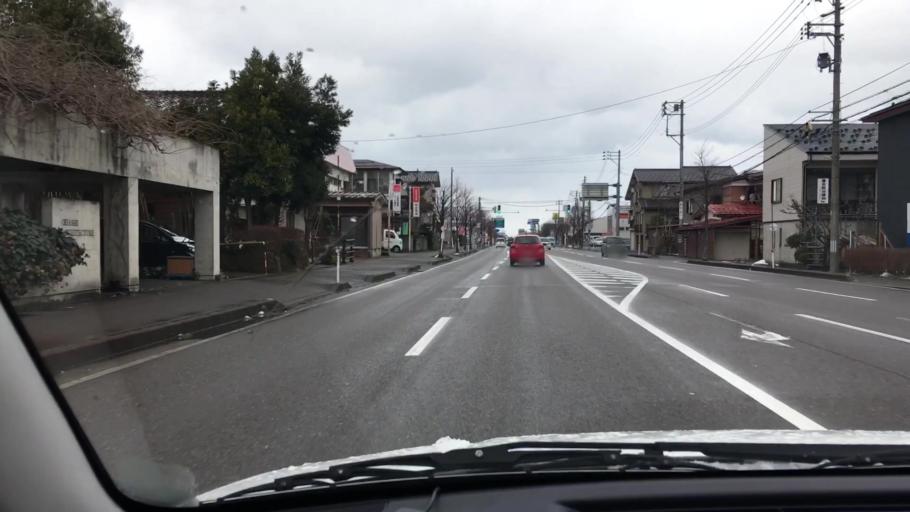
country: JP
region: Niigata
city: Joetsu
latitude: 37.1444
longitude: 138.2285
